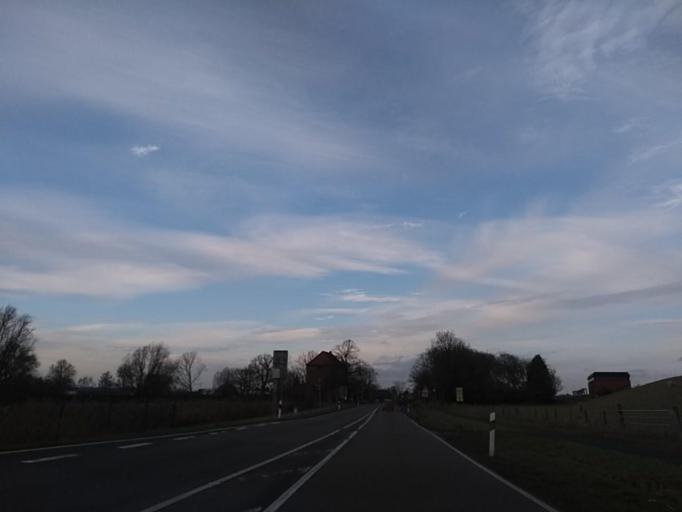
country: DE
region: Lower Saxony
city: Jemgum
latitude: 53.2310
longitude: 7.3982
